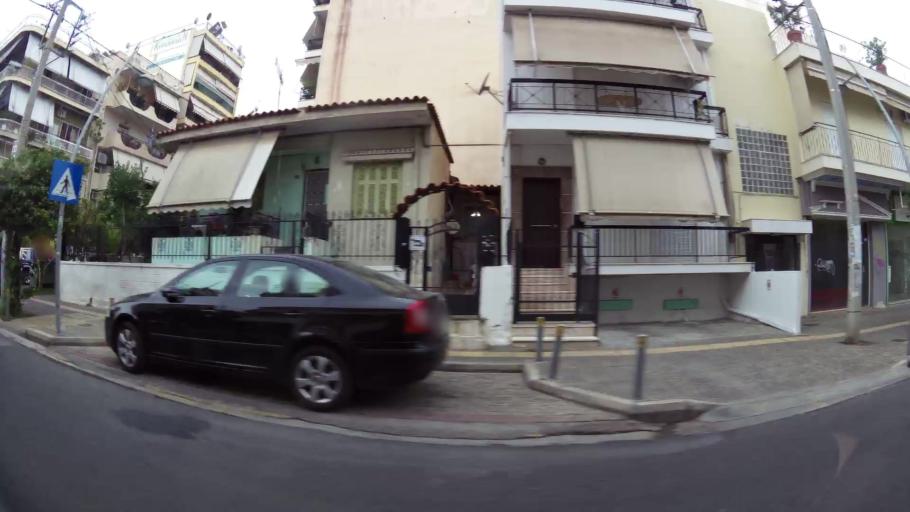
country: GR
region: Attica
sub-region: Nomos Piraios
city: Korydallos
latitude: 37.9817
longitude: 23.6388
